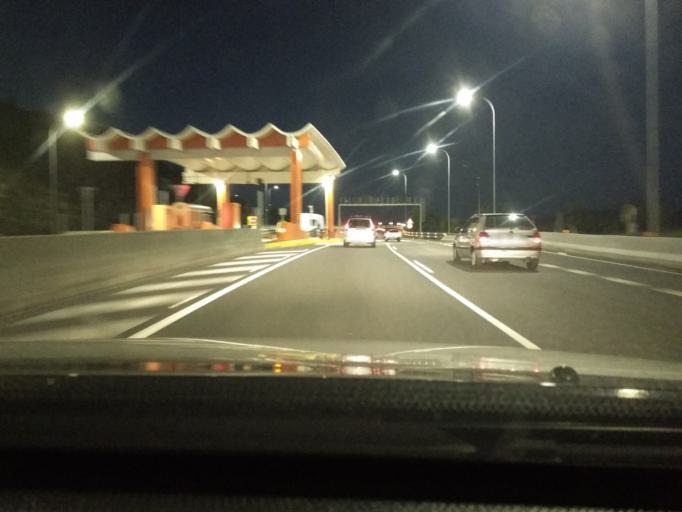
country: ES
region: Galicia
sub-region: Provincia de Pontevedra
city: Redondela
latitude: 42.2928
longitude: -8.6587
